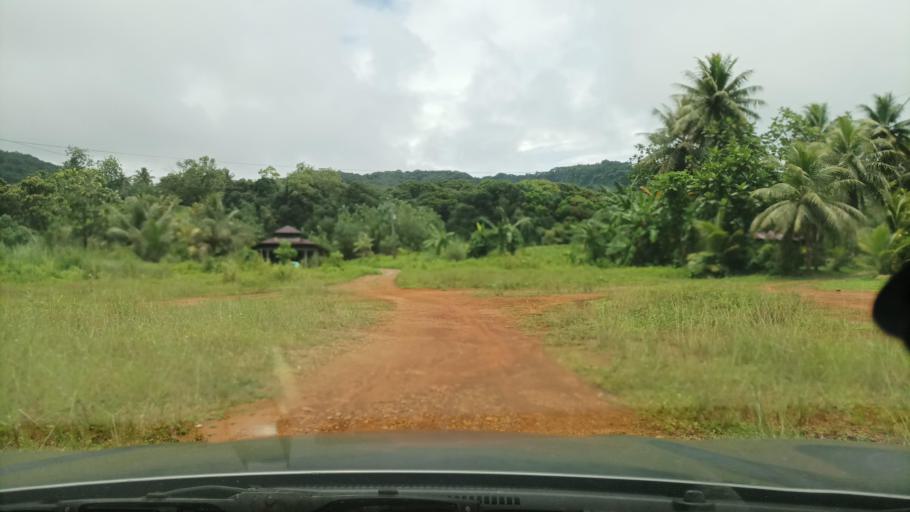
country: FM
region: Pohnpei
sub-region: Madolenihm Municipality
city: Madolenihm Municipality Government
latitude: 6.8888
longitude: 158.2918
